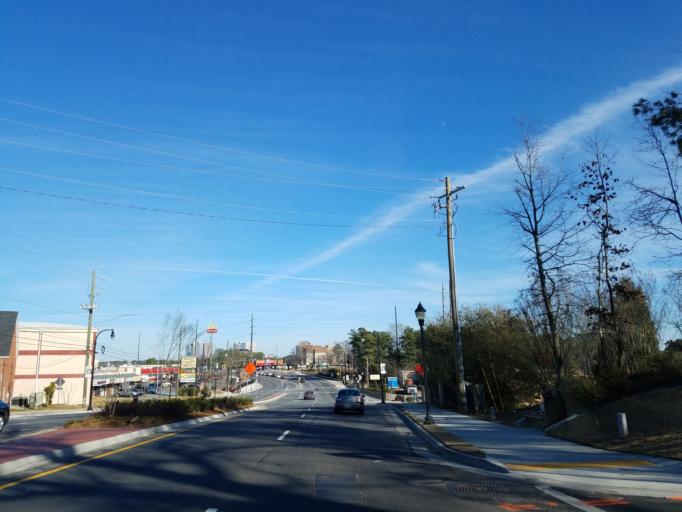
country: US
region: Georgia
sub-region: Cobb County
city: Vinings
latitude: 33.8832
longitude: -84.4794
